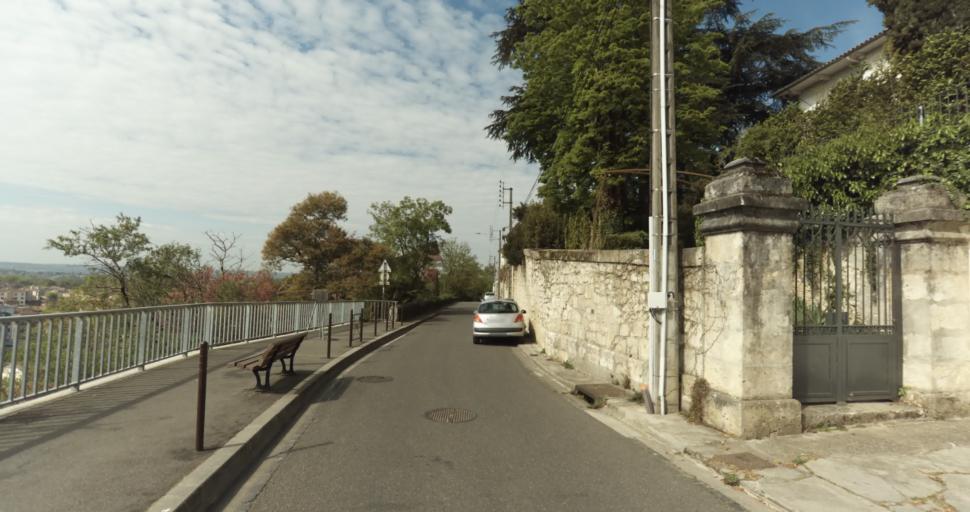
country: FR
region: Aquitaine
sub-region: Departement du Lot-et-Garonne
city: Le Passage
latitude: 44.2097
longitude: 0.6172
